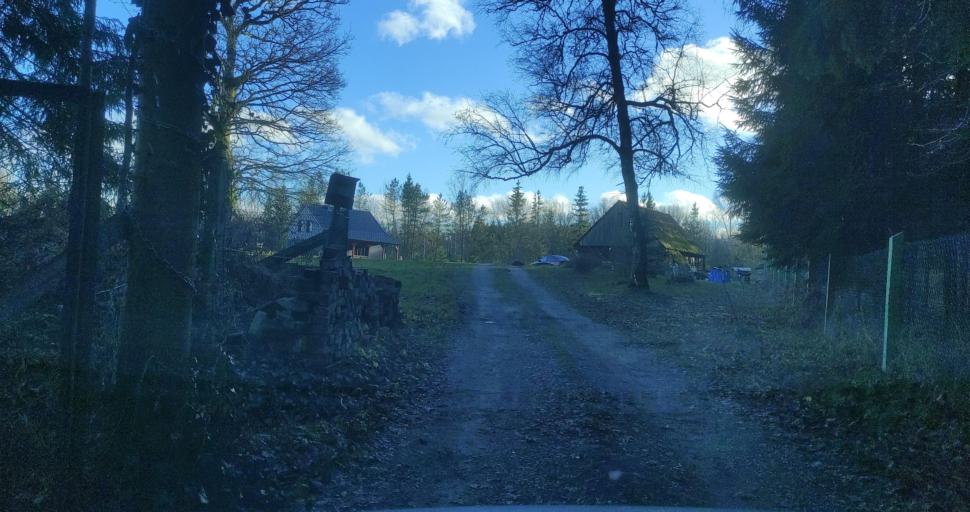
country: LV
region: Kuldigas Rajons
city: Kuldiga
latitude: 56.9071
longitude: 21.9078
